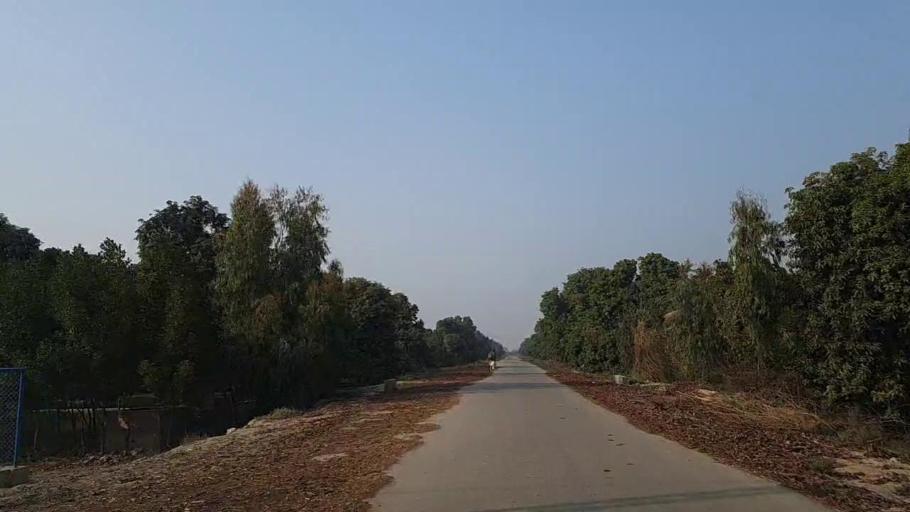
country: PK
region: Sindh
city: Sann
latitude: 26.1055
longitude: 68.1512
